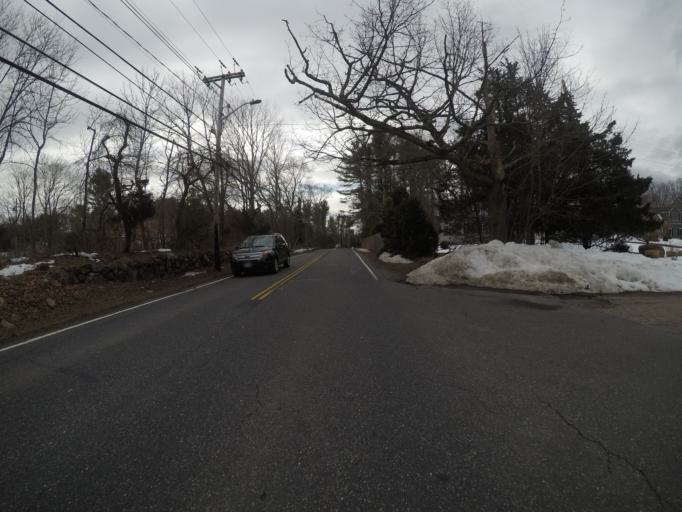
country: US
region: Massachusetts
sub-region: Bristol County
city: Easton
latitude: 42.0615
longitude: -71.1326
